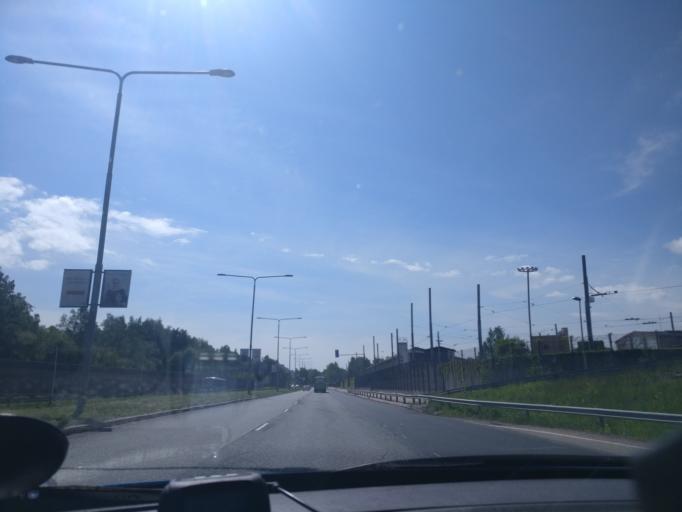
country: FI
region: Uusimaa
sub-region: Helsinki
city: Helsinki
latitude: 60.2163
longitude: 24.9737
